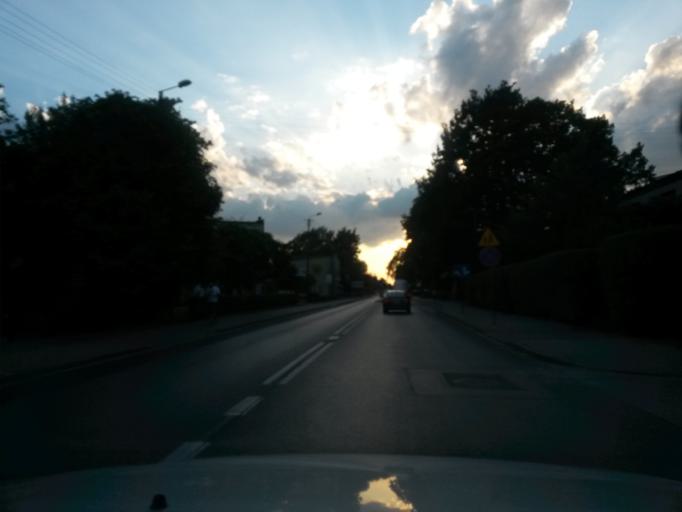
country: PL
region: Lodz Voivodeship
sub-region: Powiat wielunski
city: Wielun
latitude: 51.2258
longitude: 18.5611
